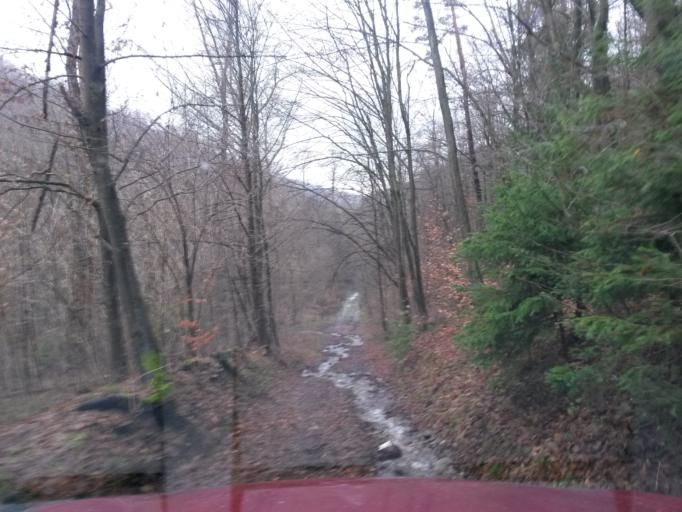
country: SK
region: Kosicky
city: Dobsina
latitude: 48.7463
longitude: 20.4063
